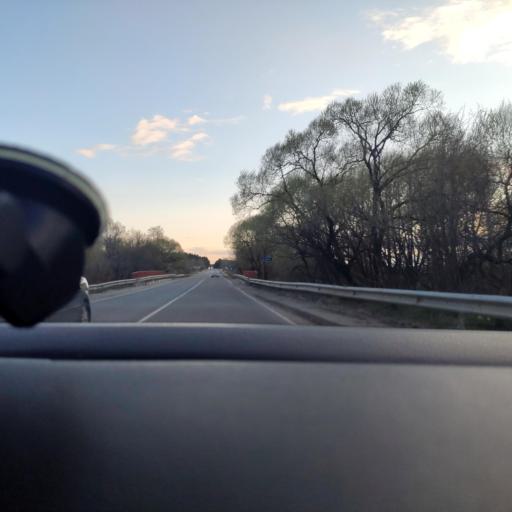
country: RU
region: Moskovskaya
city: Krasnyy Tkach
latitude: 55.4250
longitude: 39.1905
